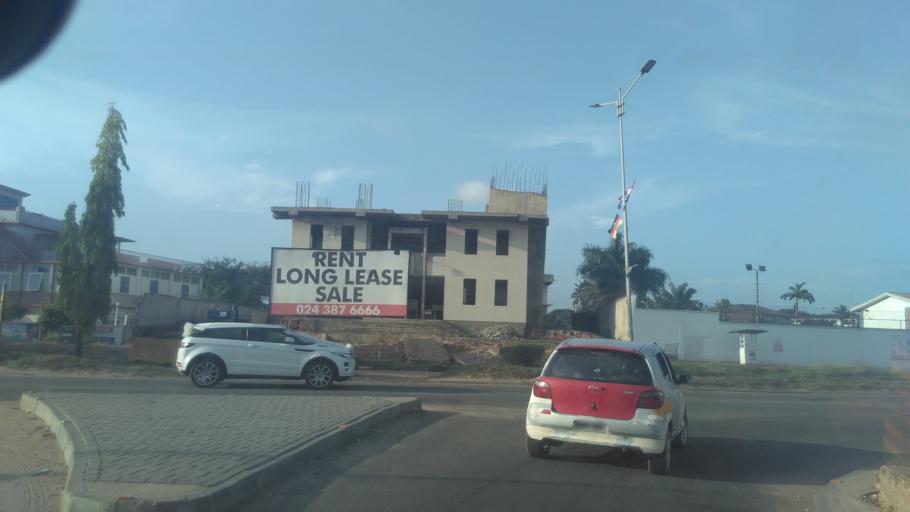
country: GH
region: Greater Accra
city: Accra
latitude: 5.5723
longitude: -0.2034
